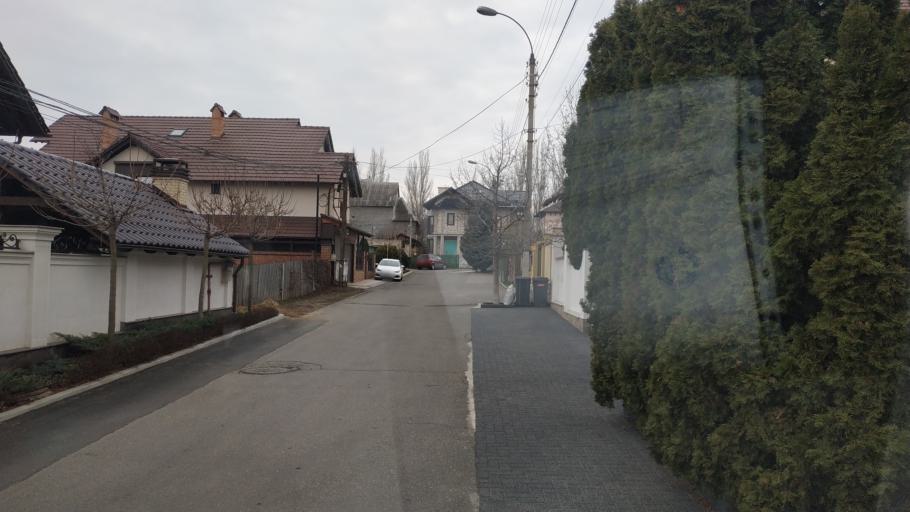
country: MD
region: Chisinau
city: Vatra
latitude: 47.0331
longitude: 28.7843
